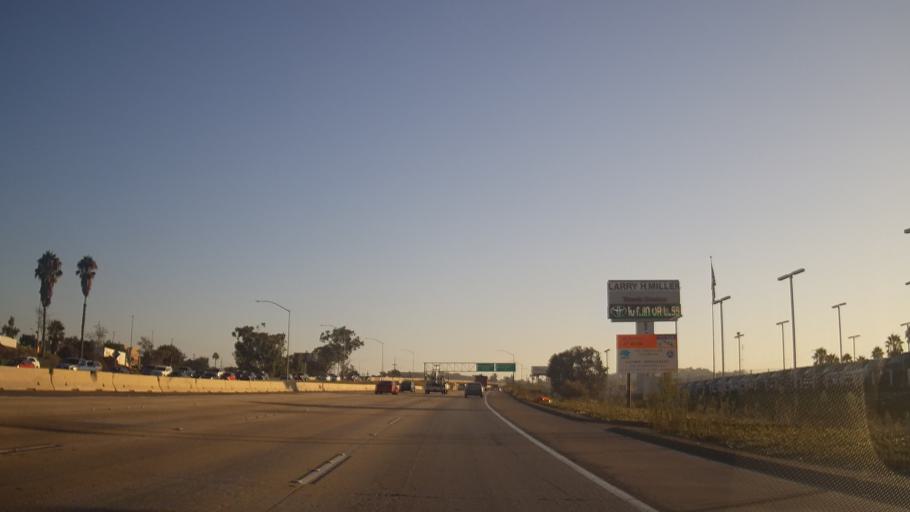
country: US
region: California
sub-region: San Diego County
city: Lemon Grove
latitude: 32.7401
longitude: -117.0526
